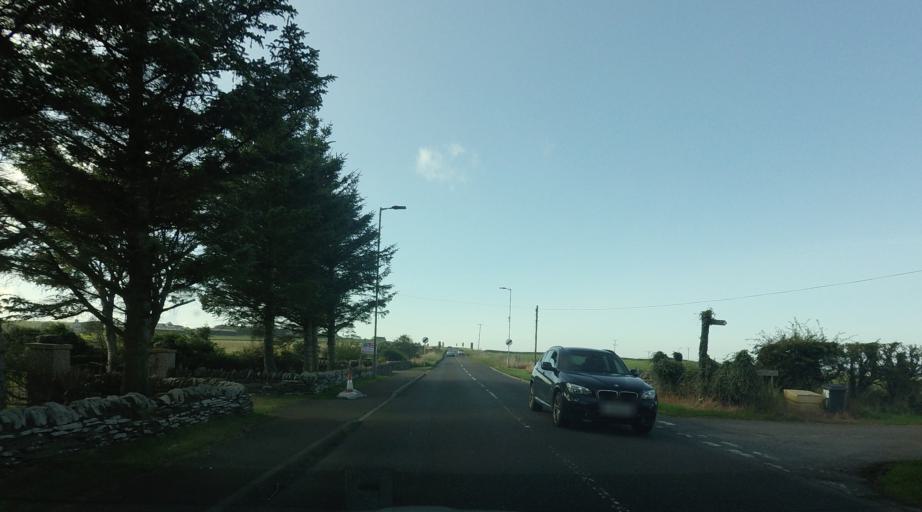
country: GB
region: Scotland
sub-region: Highland
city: Thurso
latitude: 58.5954
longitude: -3.4035
